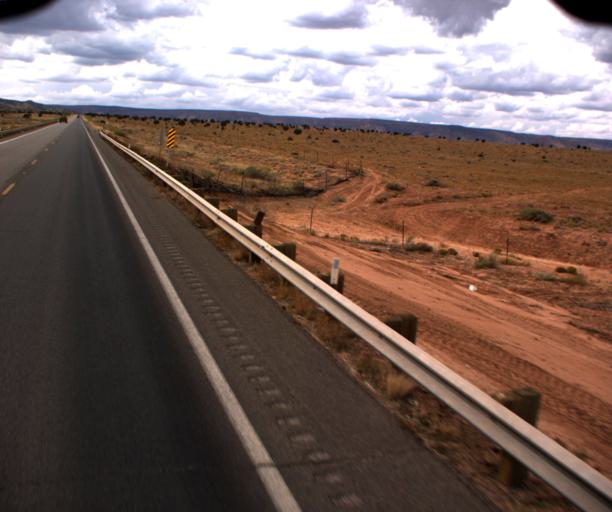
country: US
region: Arizona
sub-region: Navajo County
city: Kayenta
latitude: 36.7025
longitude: -110.2819
